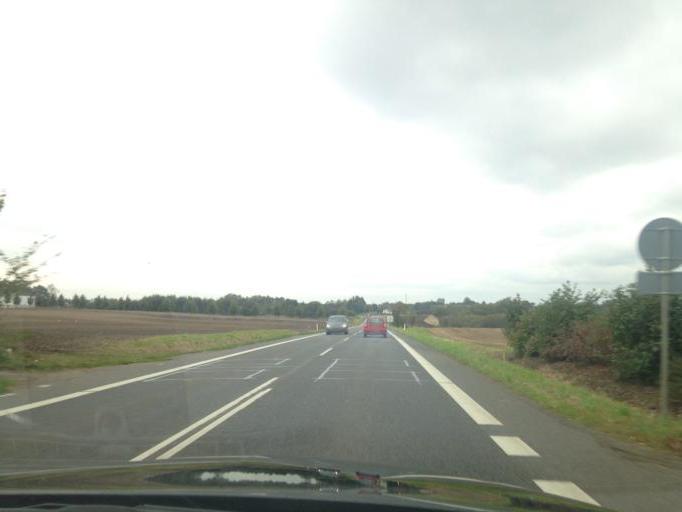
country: DK
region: South Denmark
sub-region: Kolding Kommune
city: Kolding
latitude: 55.4395
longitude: 9.4756
